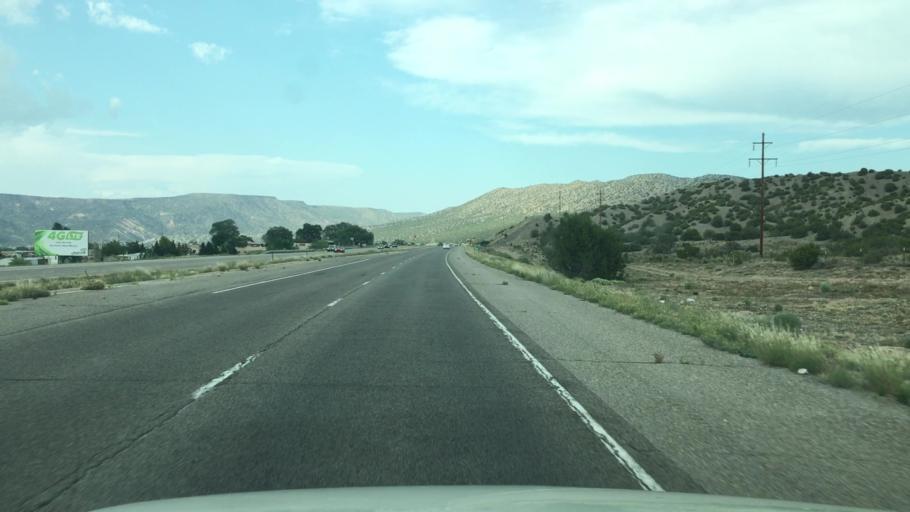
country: US
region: New Mexico
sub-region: Rio Arriba County
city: Ohkay Owingeh
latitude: 36.1417
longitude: -105.9880
